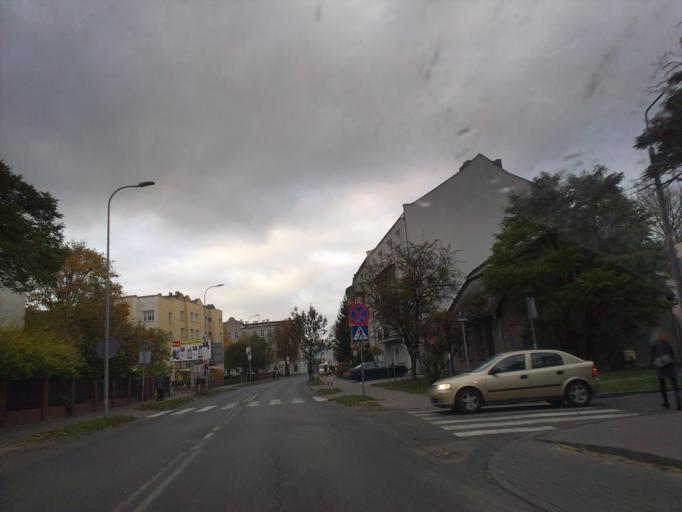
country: PL
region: Kujawsko-Pomorskie
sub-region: Torun
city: Torun
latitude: 53.0197
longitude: 18.6024
